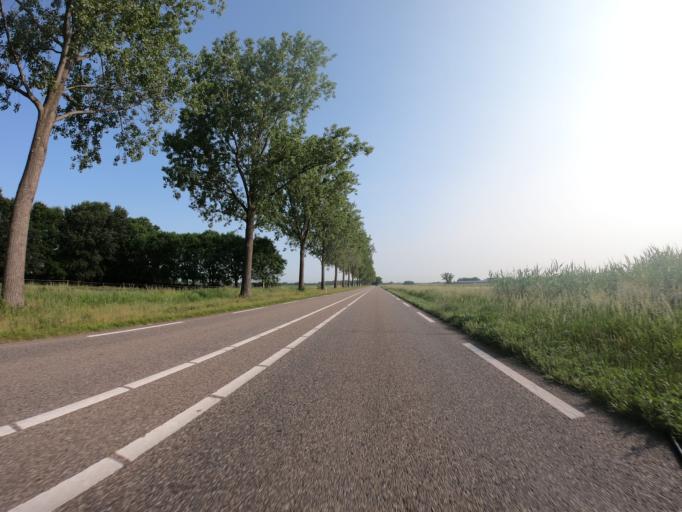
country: NL
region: North Brabant
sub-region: Gemeente Landerd
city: Reek
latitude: 51.7528
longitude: 5.6673
